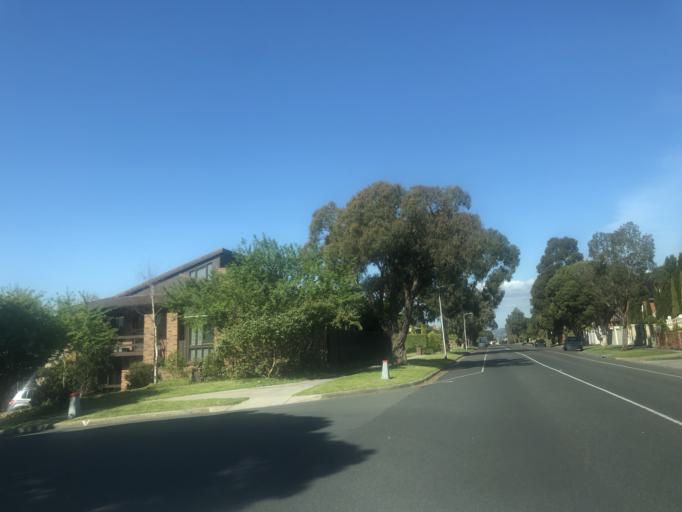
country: AU
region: Victoria
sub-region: Monash
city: Mulgrave
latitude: -37.9128
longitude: 145.1929
